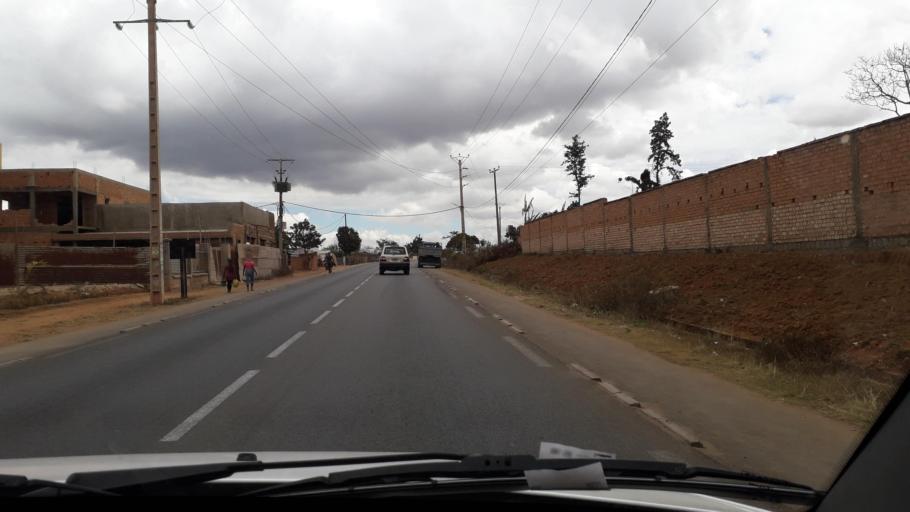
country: MG
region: Analamanga
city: Antananarivo
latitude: -18.8046
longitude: 47.4909
